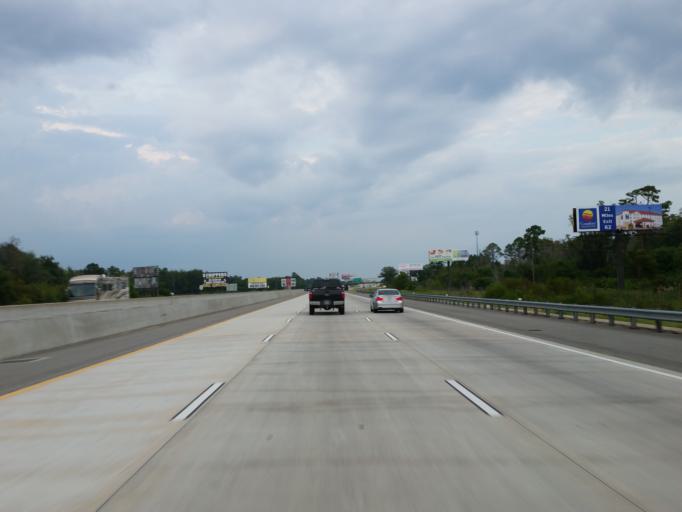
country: US
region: Georgia
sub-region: Cook County
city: Sparks
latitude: 31.1573
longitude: -83.4467
